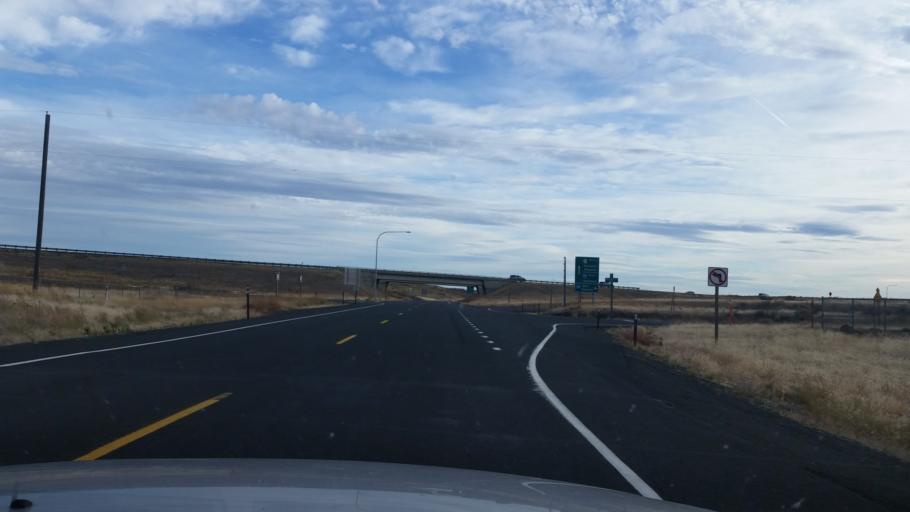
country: US
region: Washington
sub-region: Lincoln County
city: Davenport
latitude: 47.3105
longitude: -117.9729
